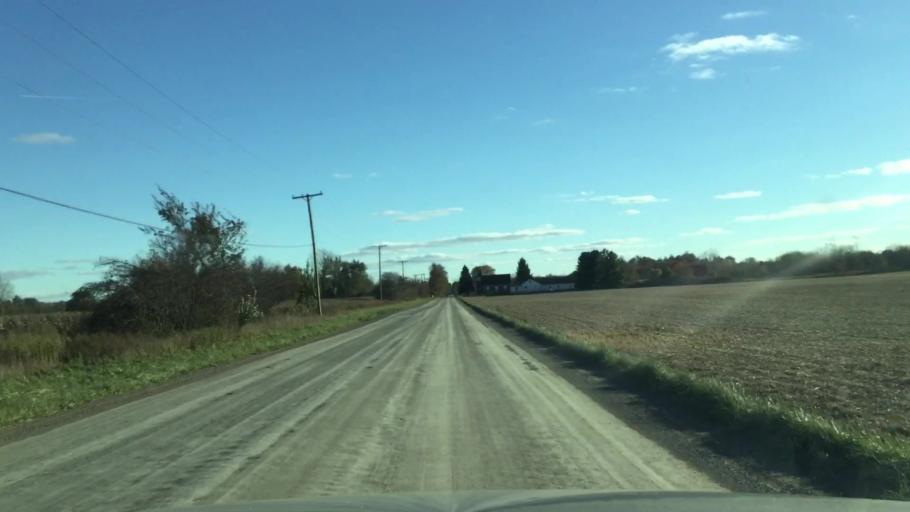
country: US
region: Michigan
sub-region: Lapeer County
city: Lapeer
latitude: 43.0715
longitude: -83.2274
